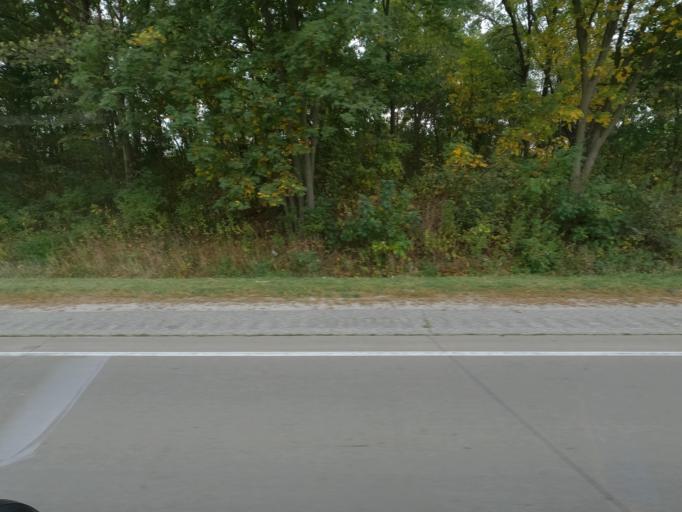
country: US
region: Iowa
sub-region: Wapello County
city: Eddyville
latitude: 41.0977
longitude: -92.5194
